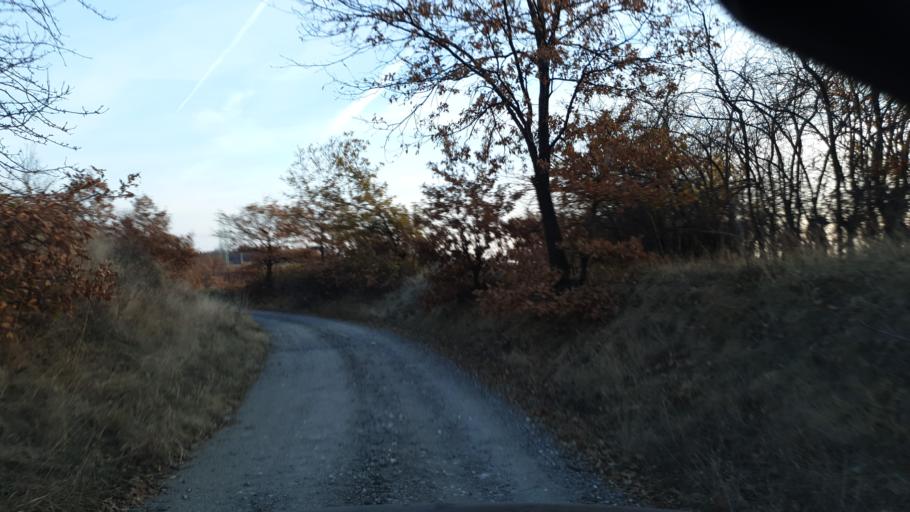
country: RS
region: Central Serbia
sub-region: Borski Okrug
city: Bor
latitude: 44.0640
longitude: 22.0797
